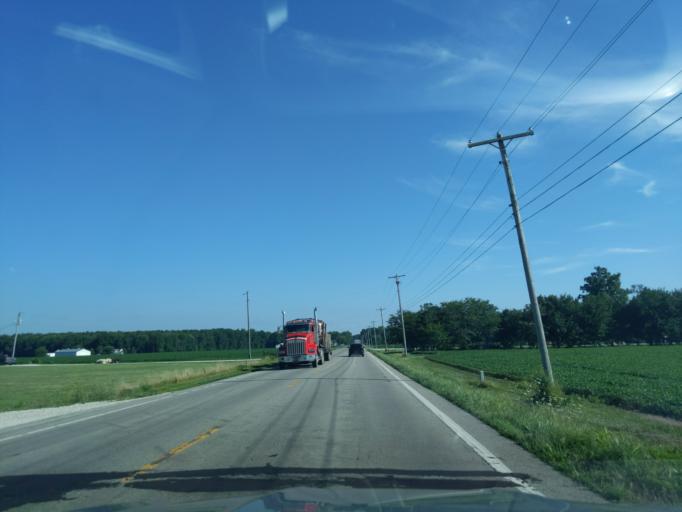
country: US
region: Indiana
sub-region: Ripley County
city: Osgood
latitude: 39.1591
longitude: -85.3061
